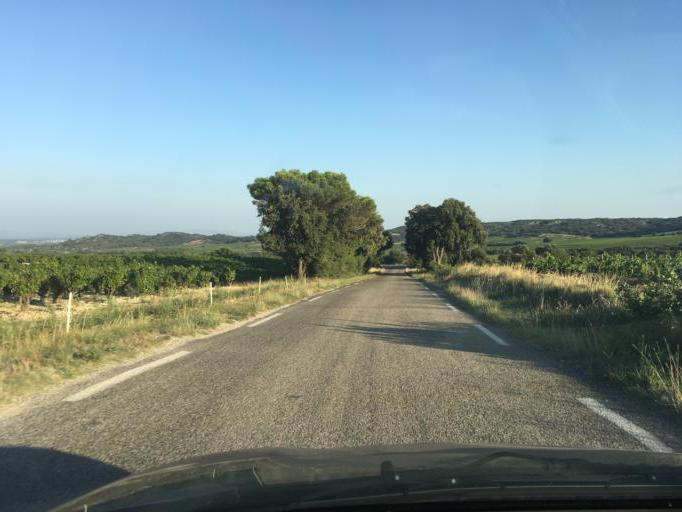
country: FR
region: Languedoc-Roussillon
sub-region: Departement du Gard
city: Tavel
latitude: 44.0137
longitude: 4.6628
